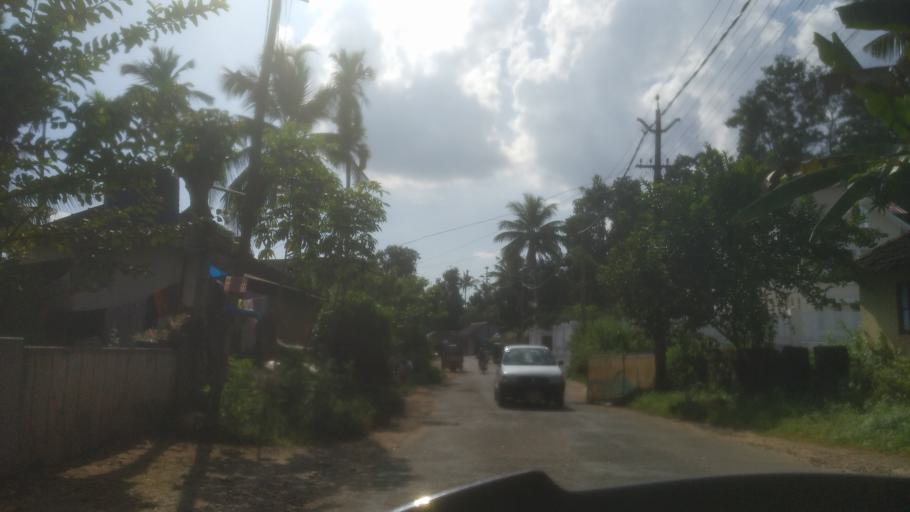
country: IN
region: Kerala
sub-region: Ernakulam
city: Muvattupula
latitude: 9.9992
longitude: 76.6282
